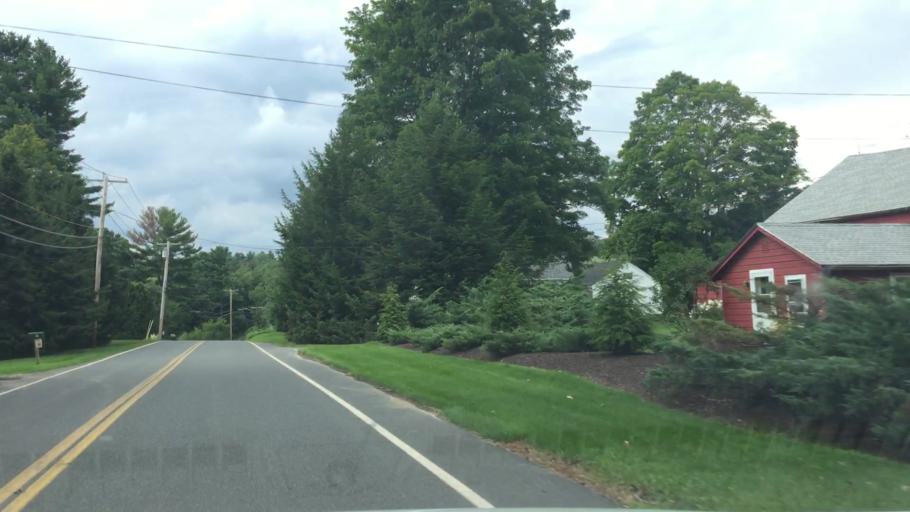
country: US
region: Massachusetts
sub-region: Berkshire County
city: Great Barrington
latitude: 42.2109
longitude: -73.3877
